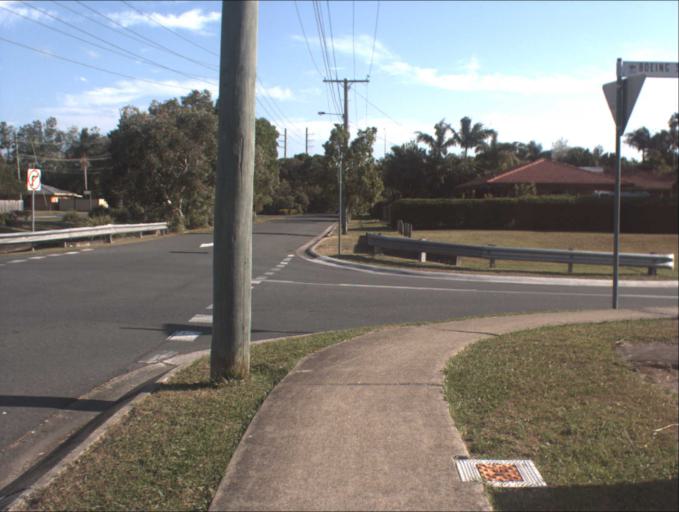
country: AU
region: Queensland
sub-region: Logan
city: Beenleigh
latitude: -27.6830
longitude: 153.1809
